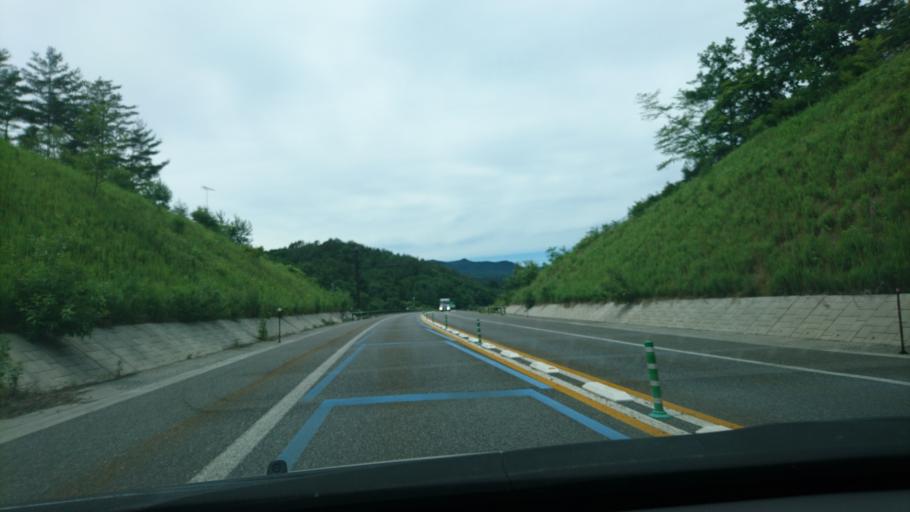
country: JP
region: Iwate
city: Miyako
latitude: 39.9328
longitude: 141.8465
